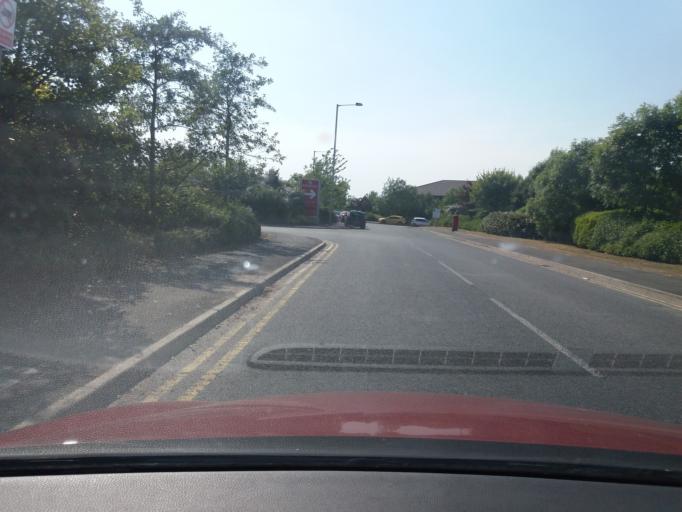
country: GB
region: England
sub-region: Lancashire
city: Clayton-le-Woods
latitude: 53.6864
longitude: -2.6701
